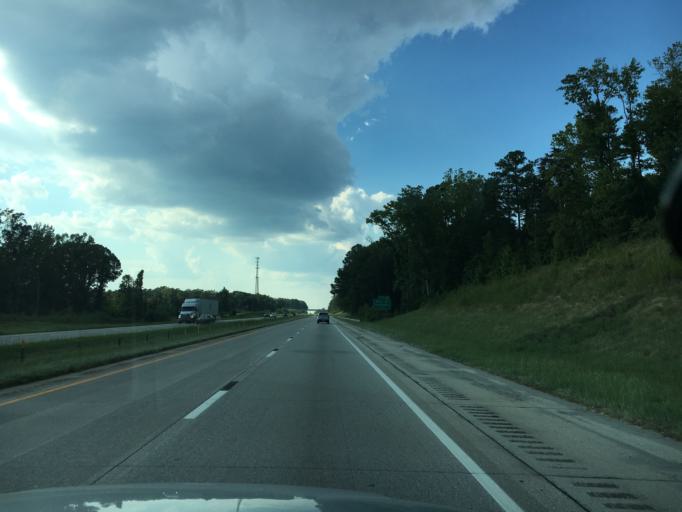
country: US
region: South Carolina
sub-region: Laurens County
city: Watts Mills
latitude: 34.5619
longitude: -82.0226
